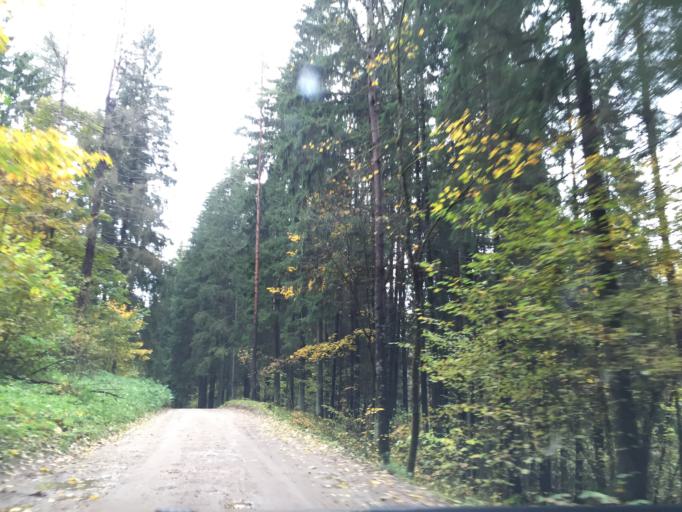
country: LV
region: Ogre
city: Ogre
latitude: 56.8052
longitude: 24.6345
